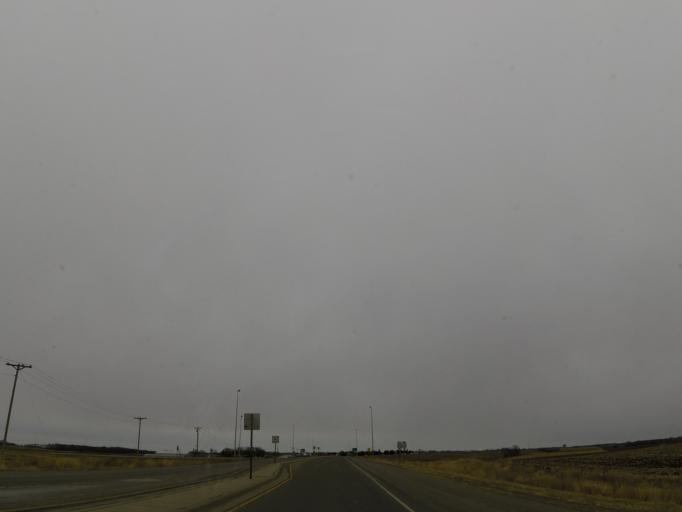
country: US
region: Minnesota
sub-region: Le Sueur County
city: Le Sueur
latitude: 44.5430
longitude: -93.8538
